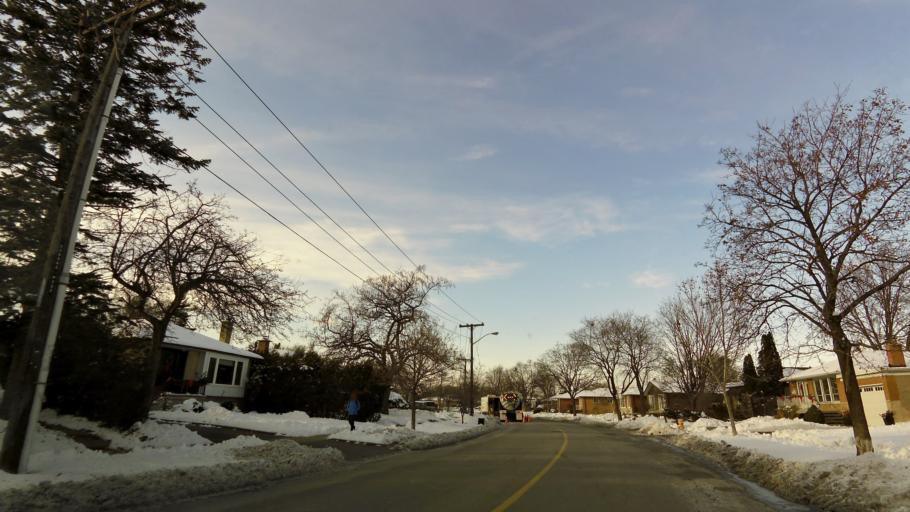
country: CA
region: Ontario
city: Etobicoke
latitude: 43.6575
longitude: -79.5776
